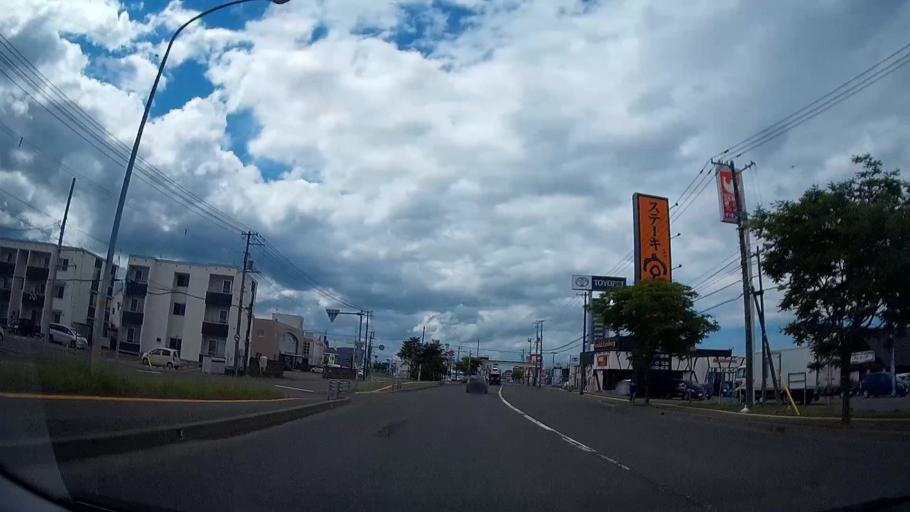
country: JP
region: Hokkaido
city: Chitose
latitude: 42.8721
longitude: 141.5860
